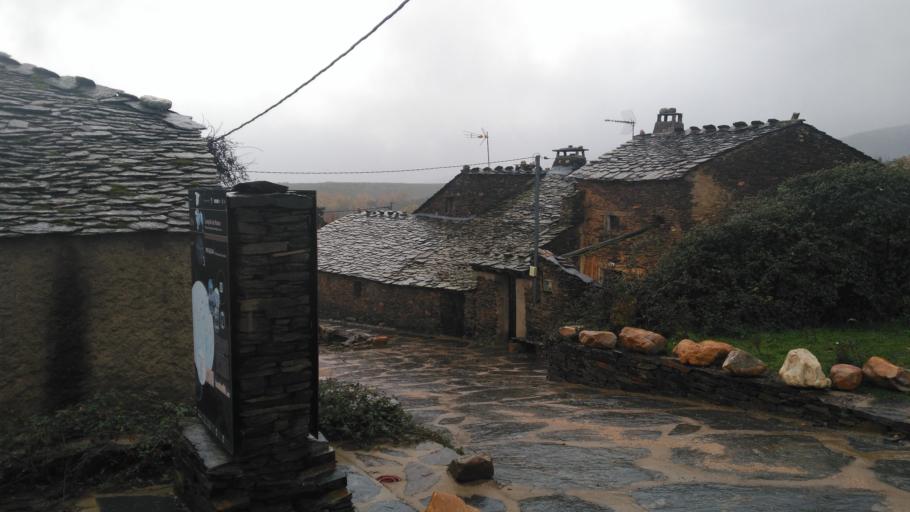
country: ES
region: Castille-La Mancha
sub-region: Provincia de Guadalajara
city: Campillo de Ranas
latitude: 41.0746
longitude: -3.3263
